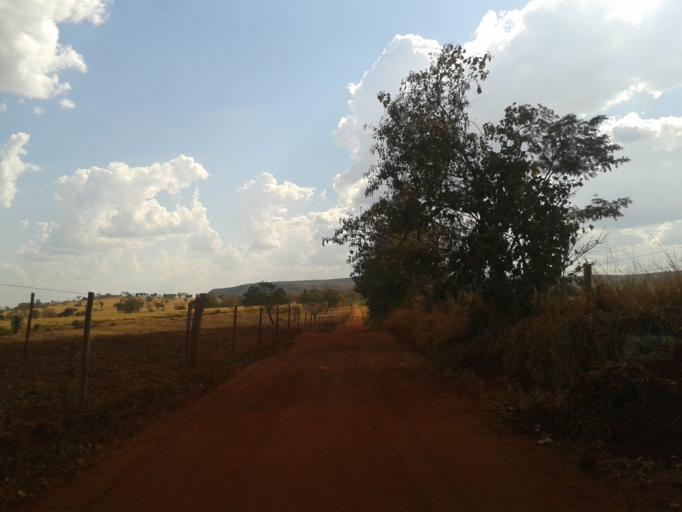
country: BR
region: Minas Gerais
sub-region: Santa Vitoria
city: Santa Vitoria
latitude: -19.2747
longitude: -50.0000
